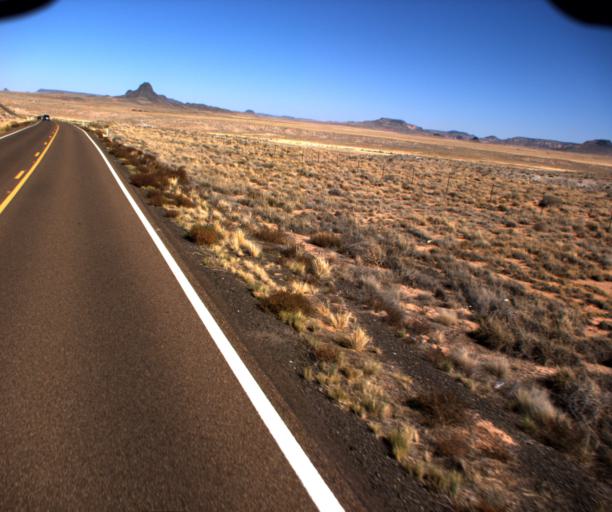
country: US
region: Arizona
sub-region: Navajo County
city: Dilkon
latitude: 35.2373
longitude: -110.4308
